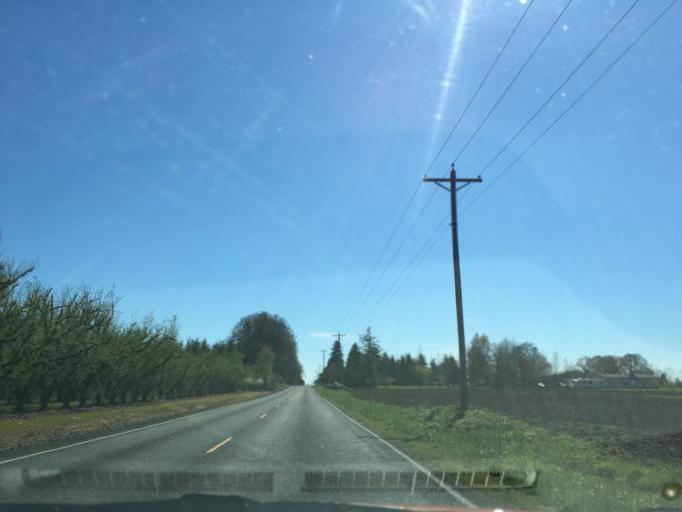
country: US
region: Oregon
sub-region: Marion County
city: Hubbard
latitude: 45.1707
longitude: -122.7226
